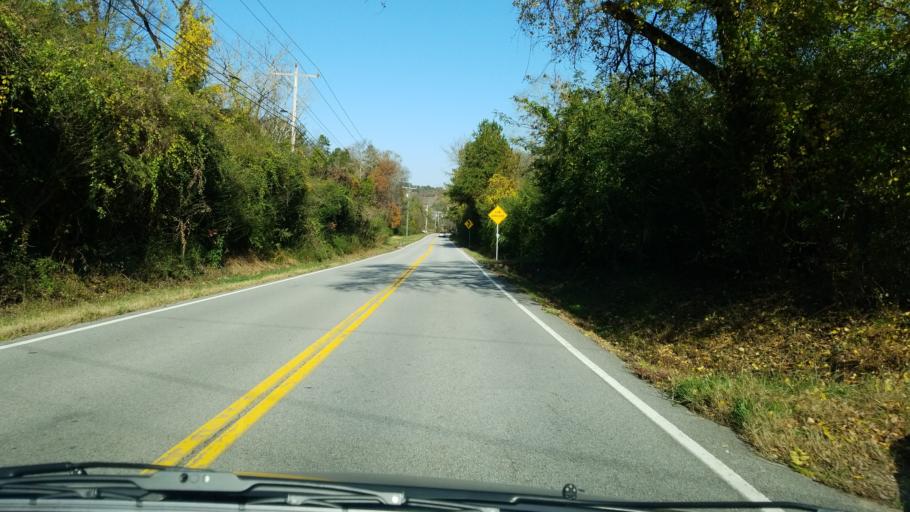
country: US
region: Tennessee
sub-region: Hamilton County
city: Harrison
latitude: 35.1245
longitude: -85.1115
